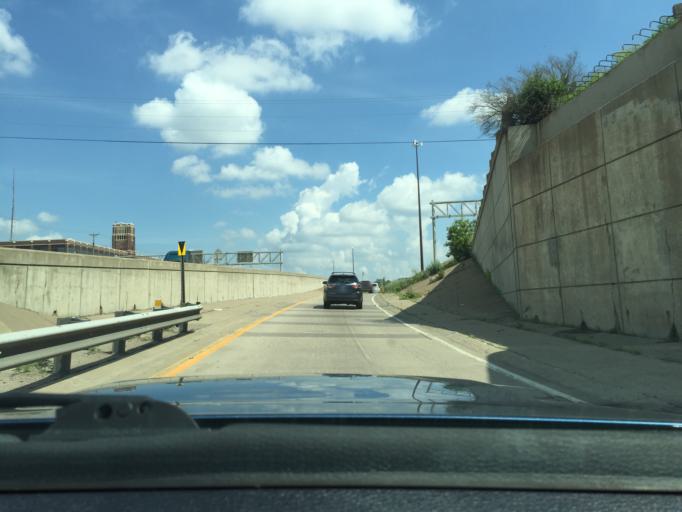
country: US
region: Minnesota
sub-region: Ramsey County
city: Lauderdale
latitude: 44.9623
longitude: -93.2019
